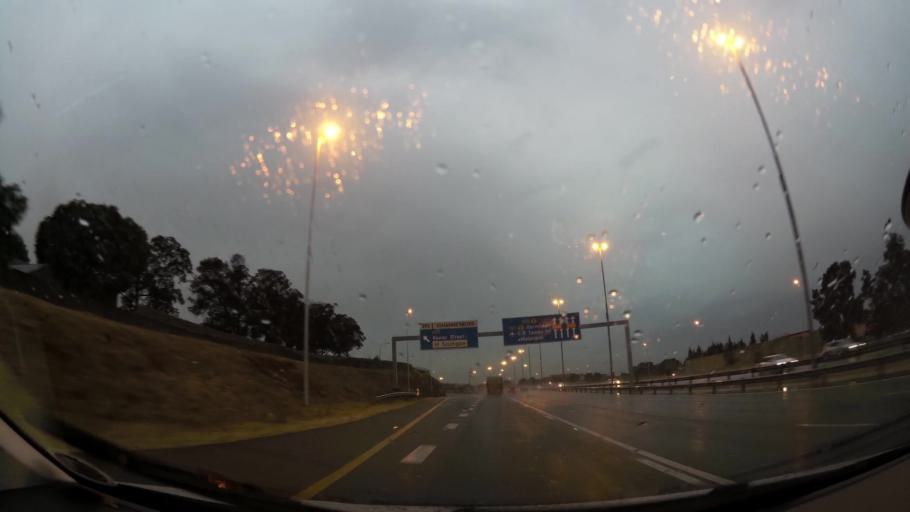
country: ZA
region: Gauteng
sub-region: City of Johannesburg Metropolitan Municipality
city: Johannesburg
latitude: -26.2603
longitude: 28.0037
